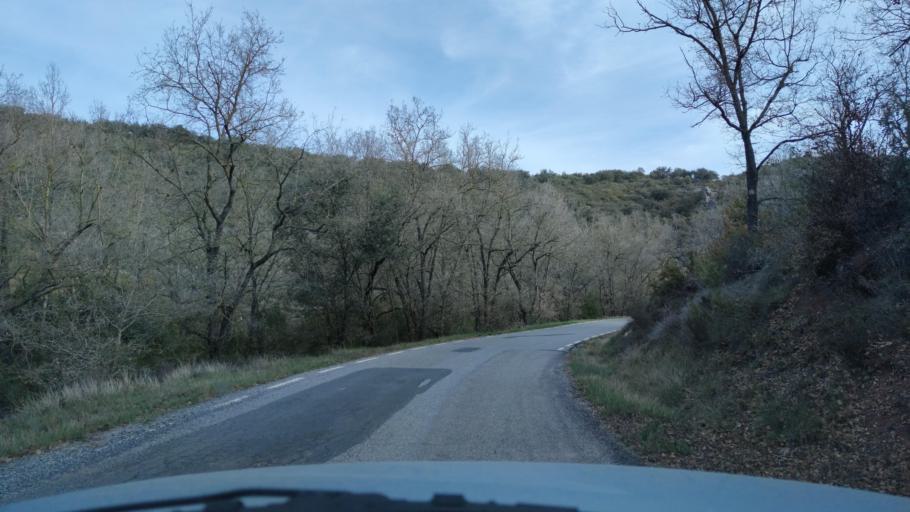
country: ES
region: Catalonia
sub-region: Provincia de Lleida
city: Os de Balaguer
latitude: 41.8862
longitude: 0.7909
